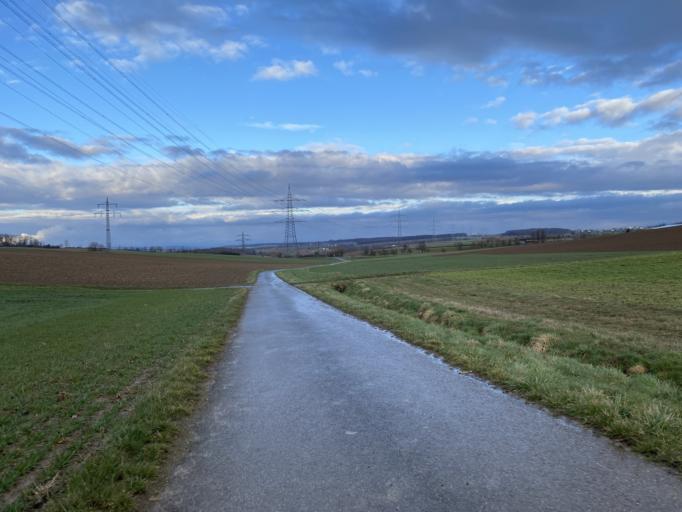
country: DE
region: Baden-Wuerttemberg
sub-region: Regierungsbezirk Stuttgart
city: Eberdingen
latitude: 48.9008
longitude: 8.9347
